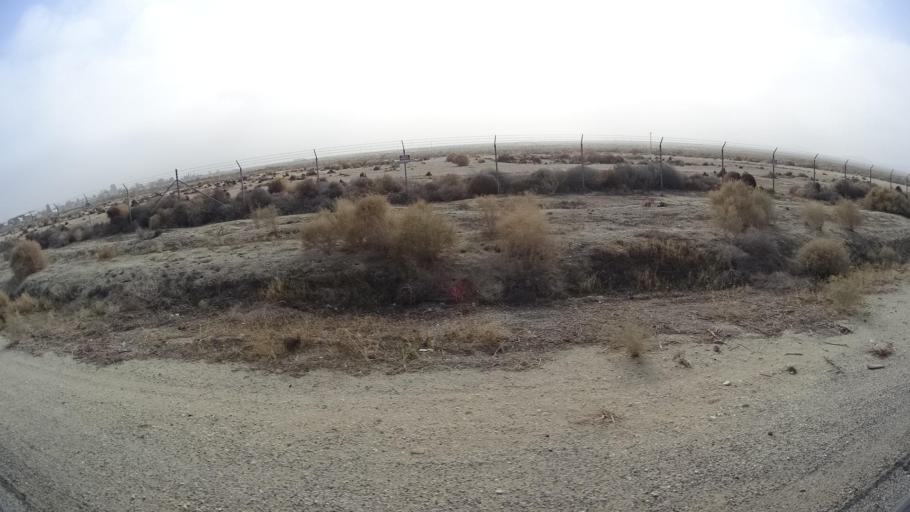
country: US
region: California
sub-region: Kern County
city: Ford City
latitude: 35.2097
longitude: -119.4163
